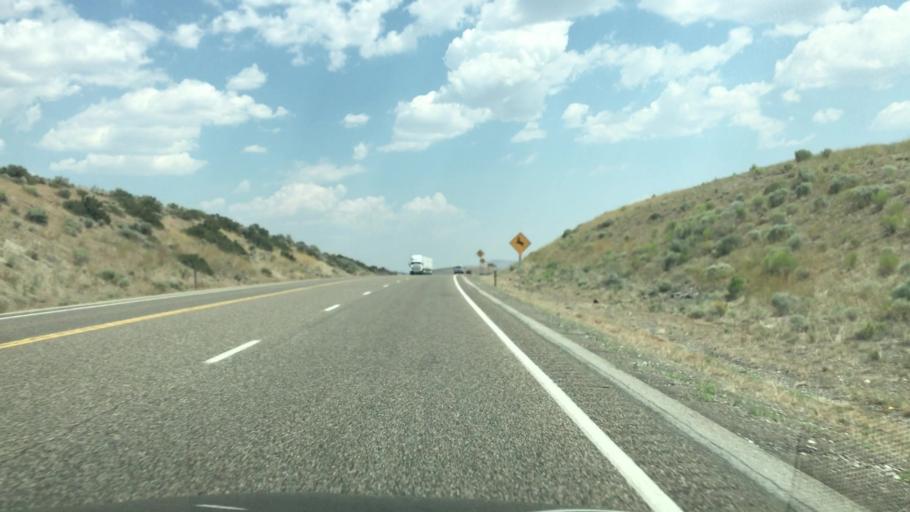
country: US
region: Nevada
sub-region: Elko County
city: Wells
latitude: 41.1910
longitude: -114.8704
